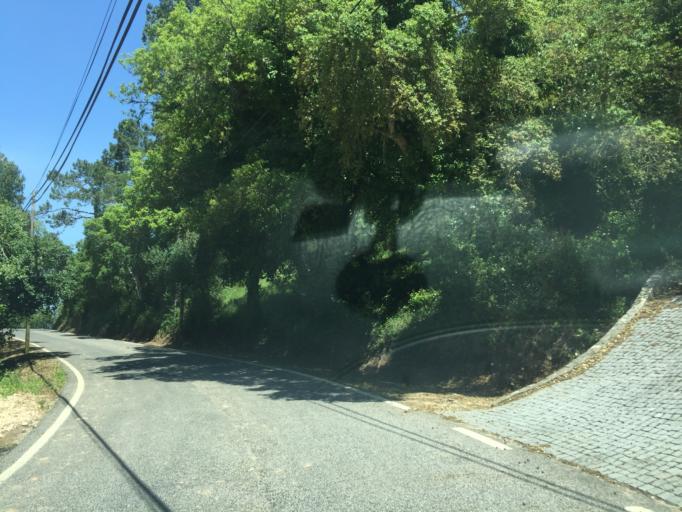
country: PT
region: Lisbon
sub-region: Mafra
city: Venda do Pinheiro
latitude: 38.8879
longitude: -9.2228
